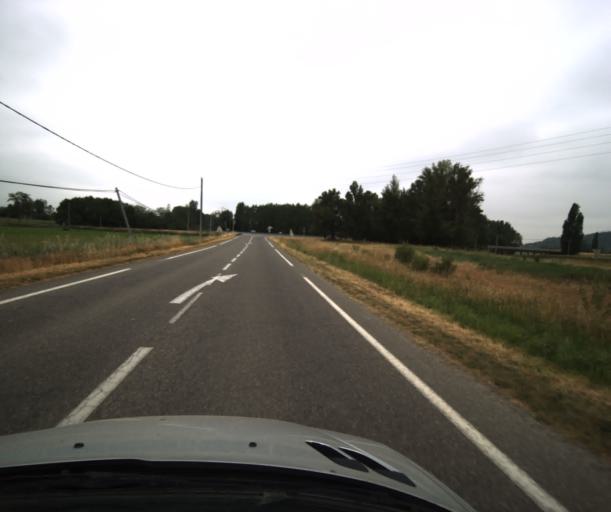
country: FR
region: Midi-Pyrenees
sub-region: Departement du Tarn-et-Garonne
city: Saint-Nicolas-de-la-Grave
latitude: 44.0755
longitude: 0.9971
